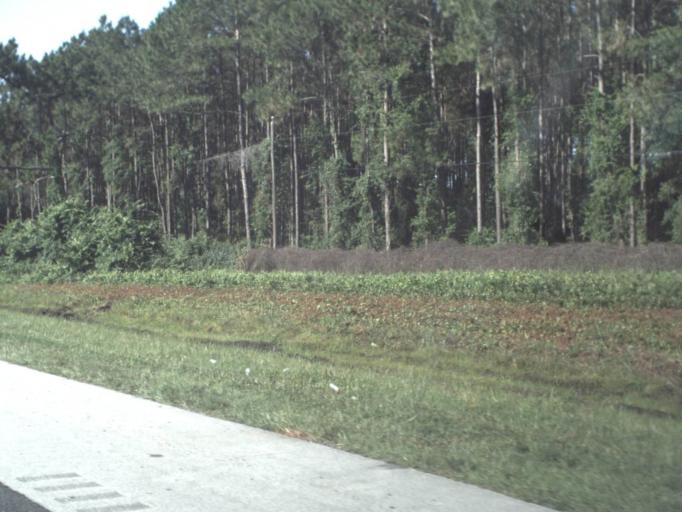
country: US
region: Florida
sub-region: Saint Johns County
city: Saint Augustine
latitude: 29.9007
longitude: -81.4071
